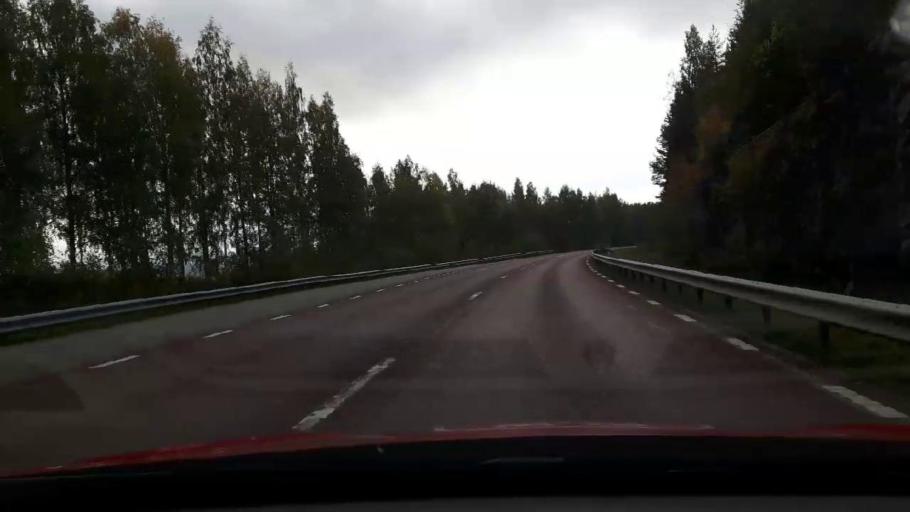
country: SE
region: Gaevleborg
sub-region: Bollnas Kommun
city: Arbra
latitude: 61.5555
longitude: 16.3475
